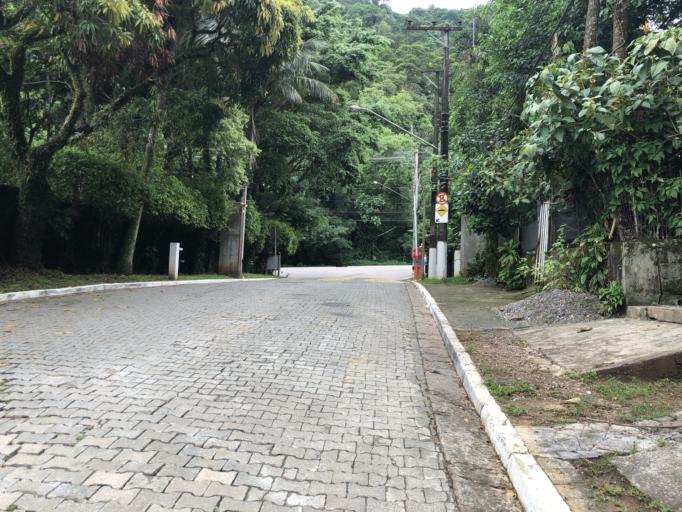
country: BR
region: Sao Paulo
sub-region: Sao Sebastiao
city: Sao Sebastiao
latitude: -23.8142
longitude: -45.5310
